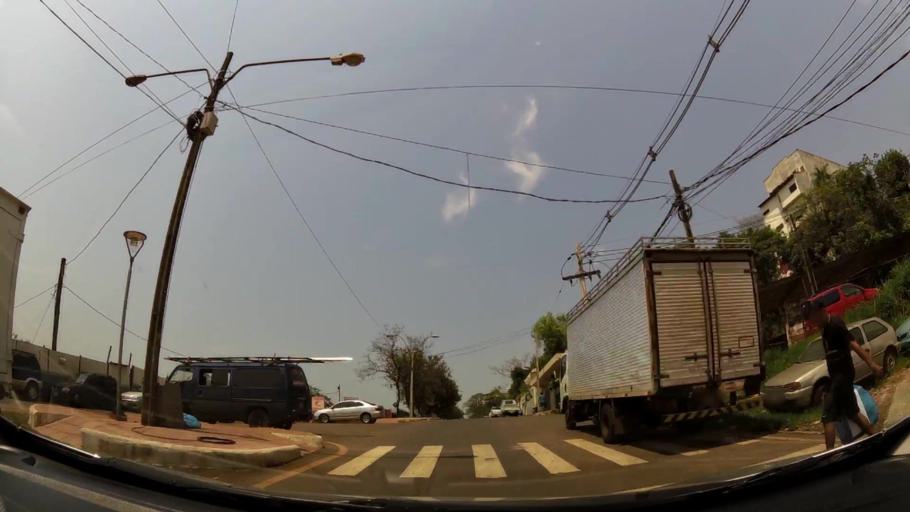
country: PY
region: Alto Parana
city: Ciudad del Este
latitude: -25.5141
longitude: -54.6068
